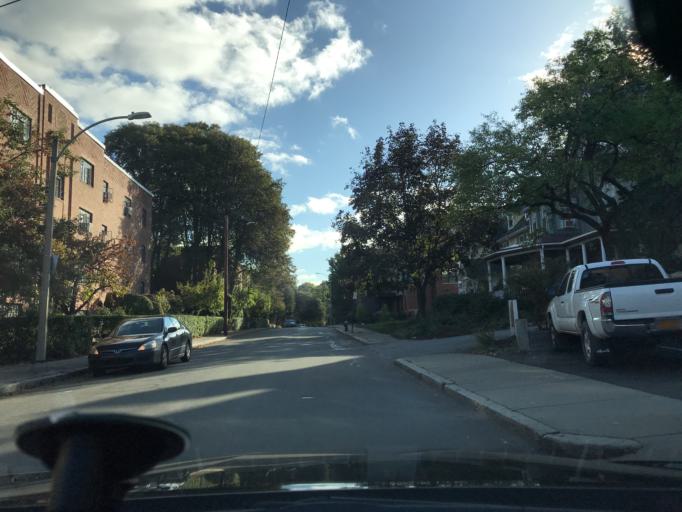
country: US
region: Massachusetts
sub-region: Norfolk County
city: Brookline
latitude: 42.3419
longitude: -71.1172
